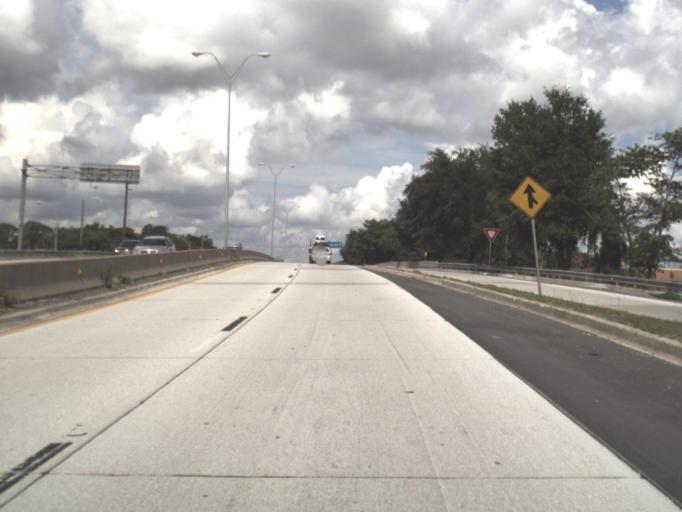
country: US
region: Florida
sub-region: Duval County
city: Jacksonville
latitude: 30.3565
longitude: -81.6524
